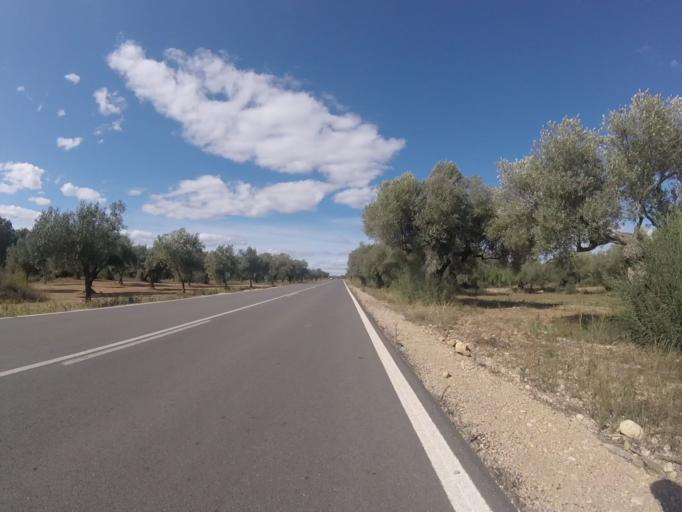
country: ES
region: Valencia
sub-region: Provincia de Castello
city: Chert/Xert
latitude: 40.4303
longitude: 0.1405
